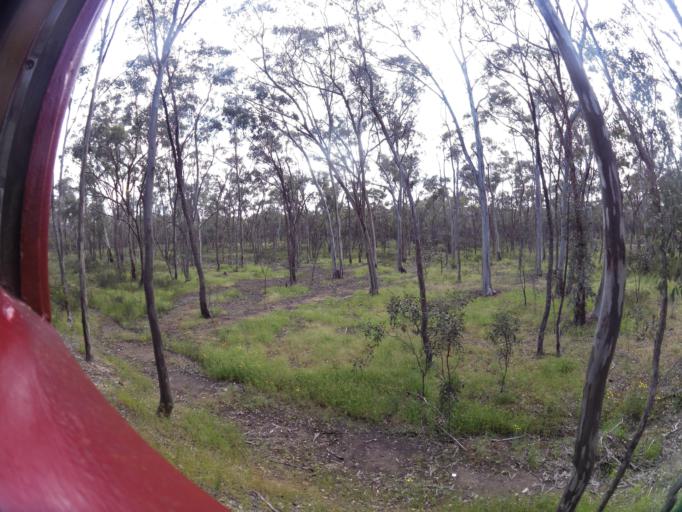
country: AU
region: Victoria
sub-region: Mount Alexander
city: Castlemaine
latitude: -37.0526
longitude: 144.1868
